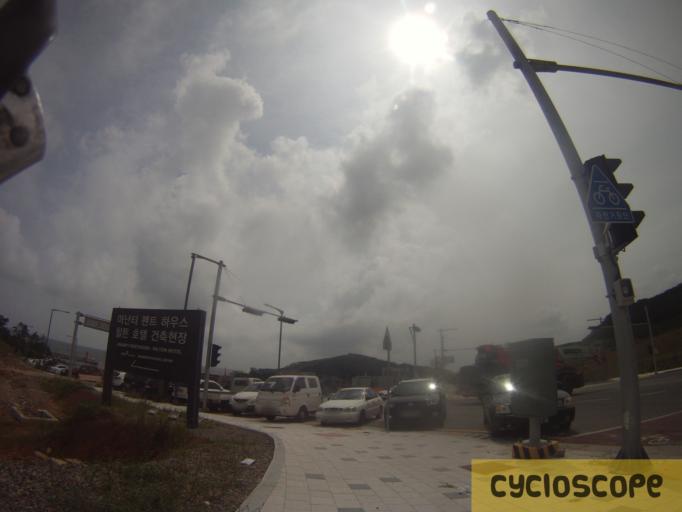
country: KR
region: Busan
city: Kijang
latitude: 35.1962
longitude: 129.2222
